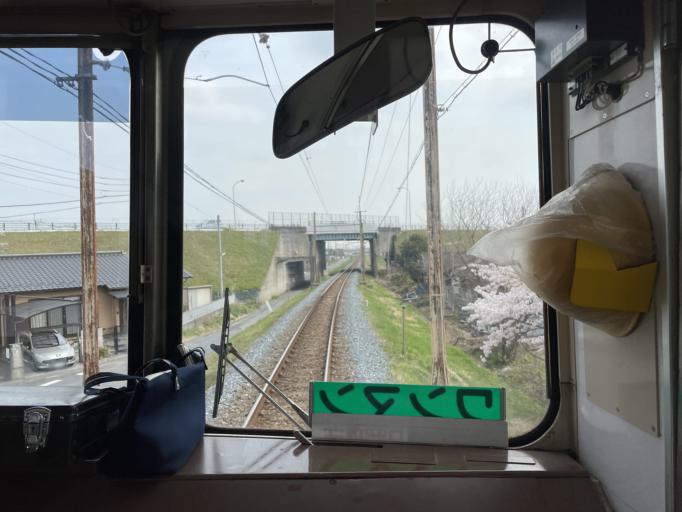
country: JP
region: Saitama
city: Kumagaya
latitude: 36.1359
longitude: 139.4018
